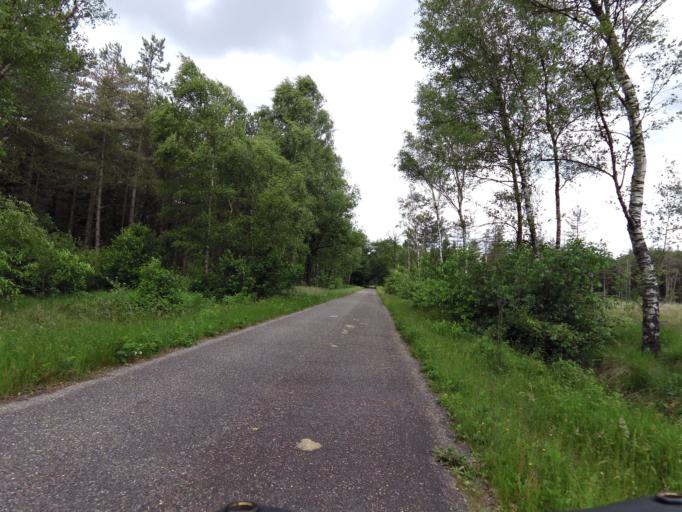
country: NL
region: North Brabant
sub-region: Gemeente Baarle-Nassau
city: Baarle-Nassau
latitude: 51.5077
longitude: 4.9006
